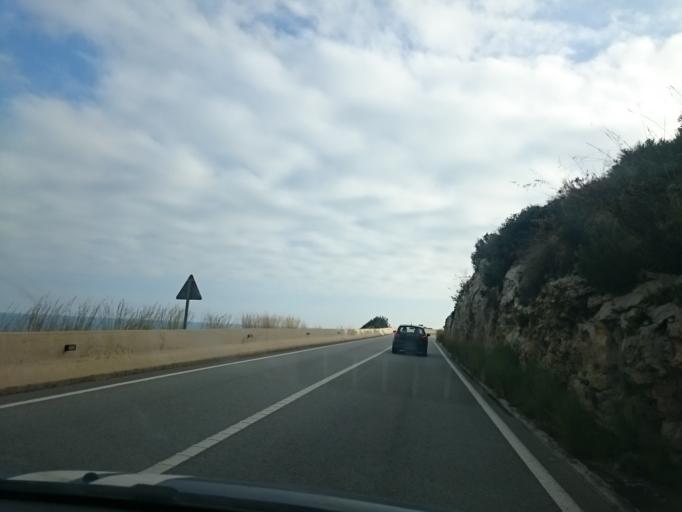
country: ES
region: Catalonia
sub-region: Provincia de Barcelona
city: Sitges
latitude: 41.2423
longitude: 1.8674
